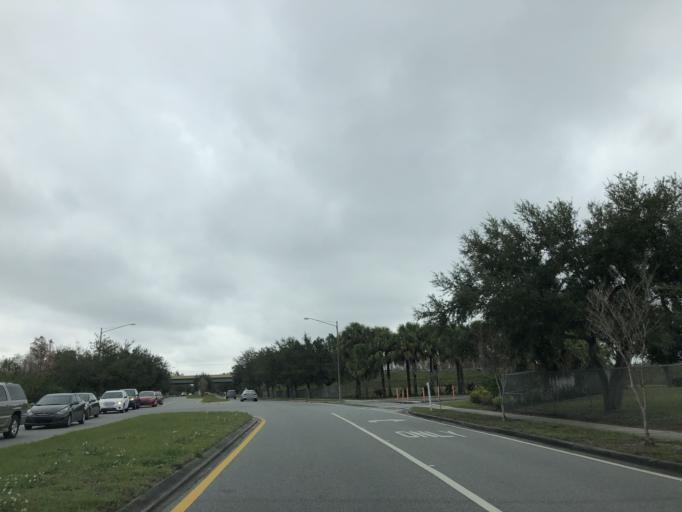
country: US
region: Florida
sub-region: Orange County
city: Hunters Creek
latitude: 28.3685
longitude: -81.3992
